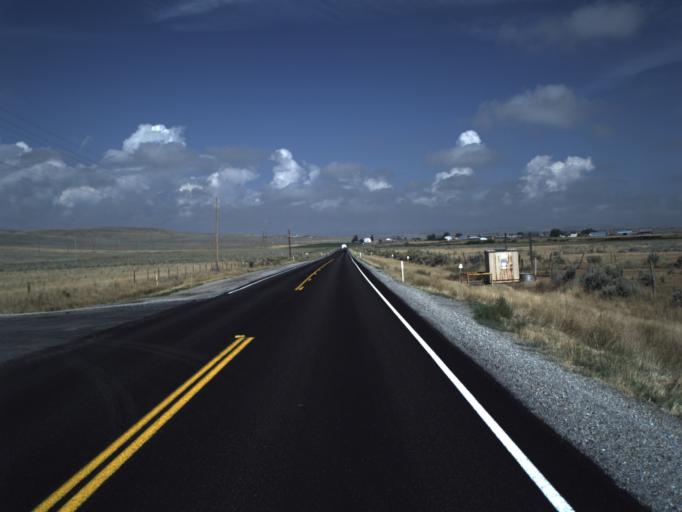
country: US
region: Utah
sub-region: Rich County
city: Randolph
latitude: 41.5869
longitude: -111.1690
